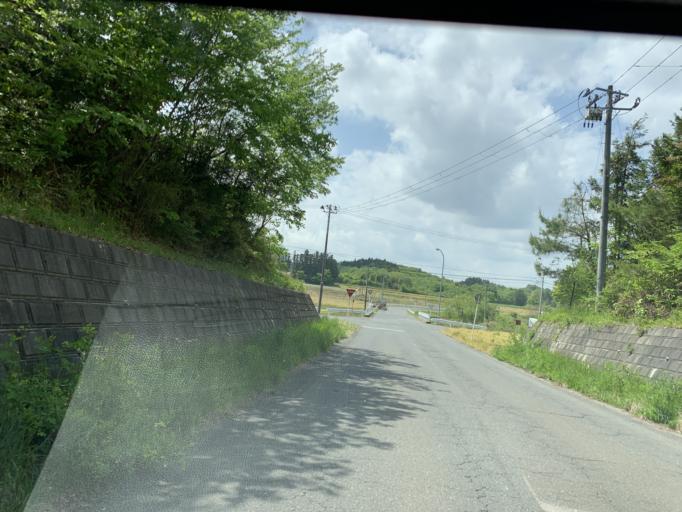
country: JP
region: Miyagi
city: Furukawa
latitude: 38.7690
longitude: 140.9535
